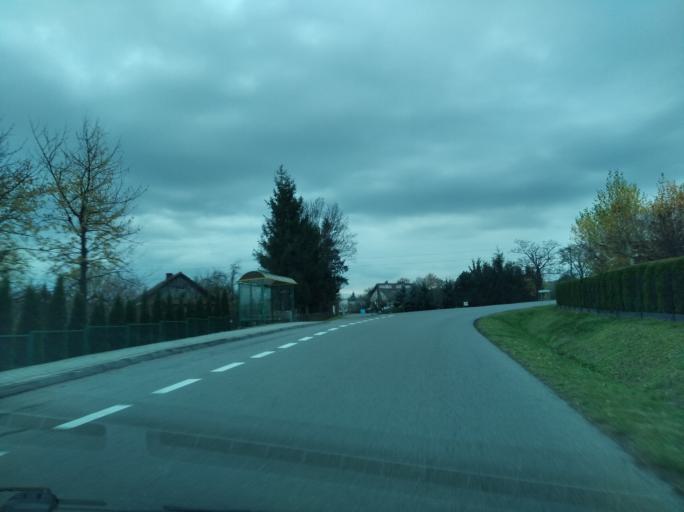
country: PL
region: Subcarpathian Voivodeship
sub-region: Powiat ropczycko-sedziszowski
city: Iwierzyce
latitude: 49.9903
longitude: 21.7279
